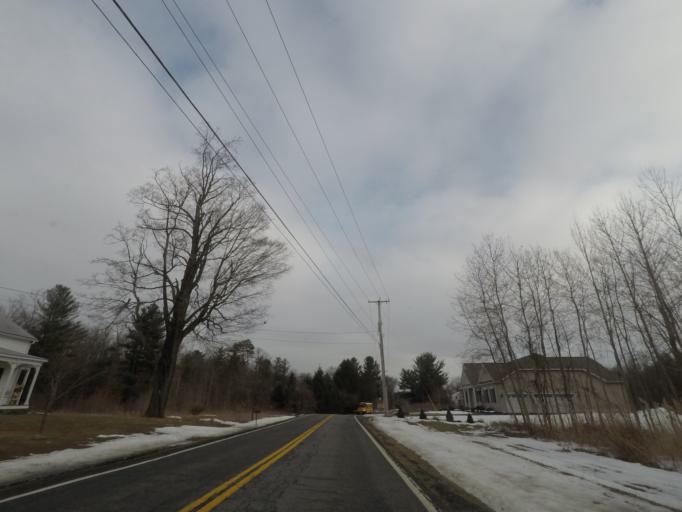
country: US
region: New York
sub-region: Schenectady County
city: Rotterdam
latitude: 42.7281
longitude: -73.9505
